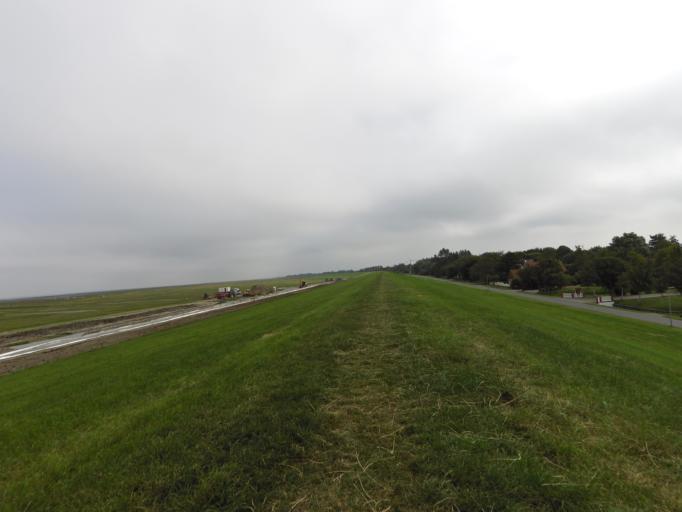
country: DE
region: Lower Saxony
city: Padingbuttel
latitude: 53.7412
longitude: 8.5220
